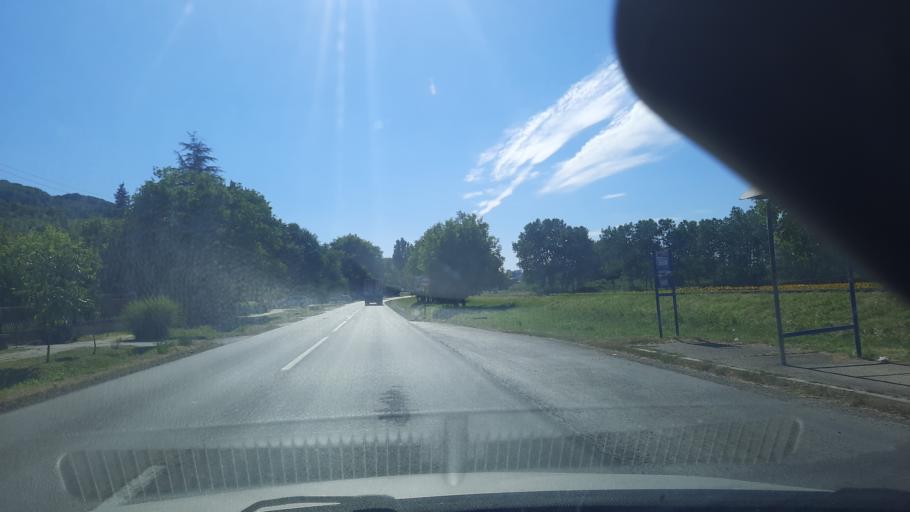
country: RS
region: Autonomna Pokrajina Vojvodina
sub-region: Juznobacki Okrug
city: Beocin
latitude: 45.2087
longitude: 19.7370
